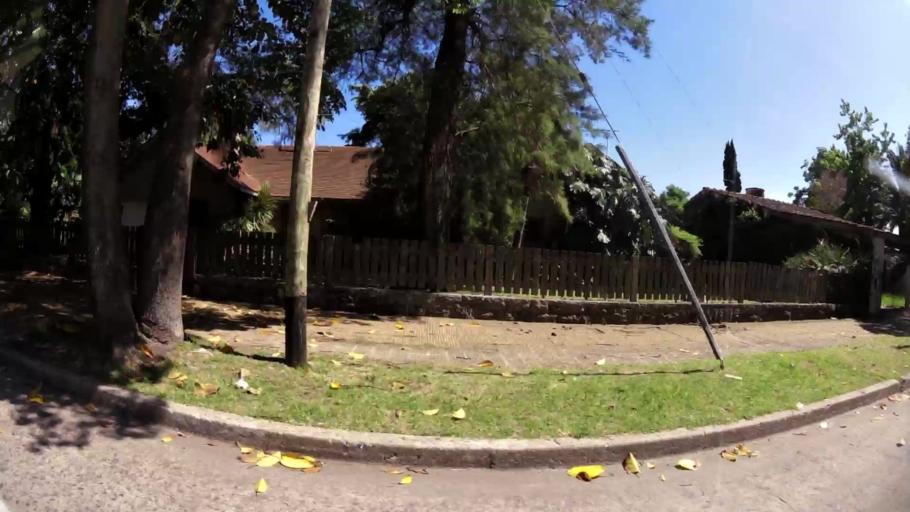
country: AR
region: Buenos Aires
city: Ituzaingo
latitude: -34.6644
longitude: -58.6649
